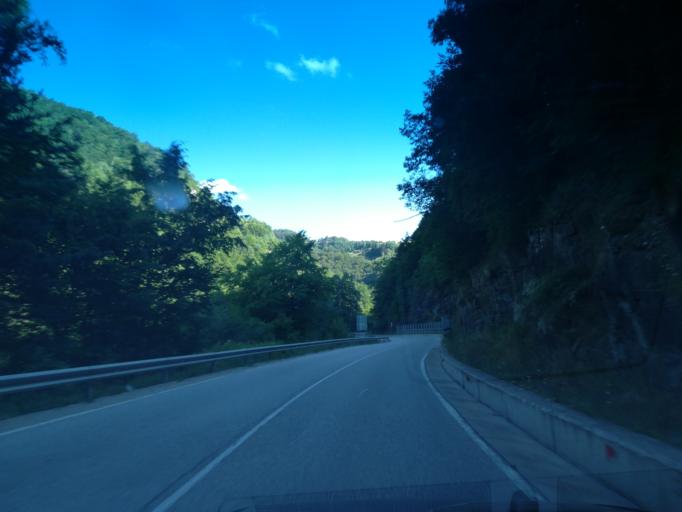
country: BG
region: Smolyan
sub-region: Obshtina Chepelare
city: Chepelare
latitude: 41.7891
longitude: 24.7093
